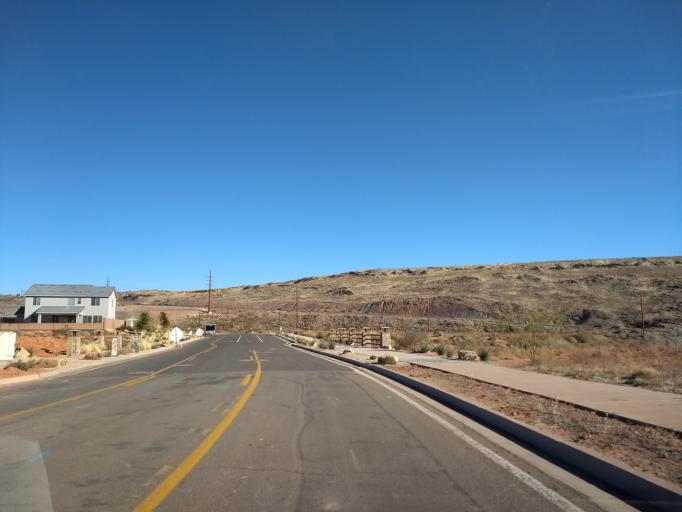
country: US
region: Utah
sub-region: Washington County
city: Washington
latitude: 37.1346
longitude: -113.4826
